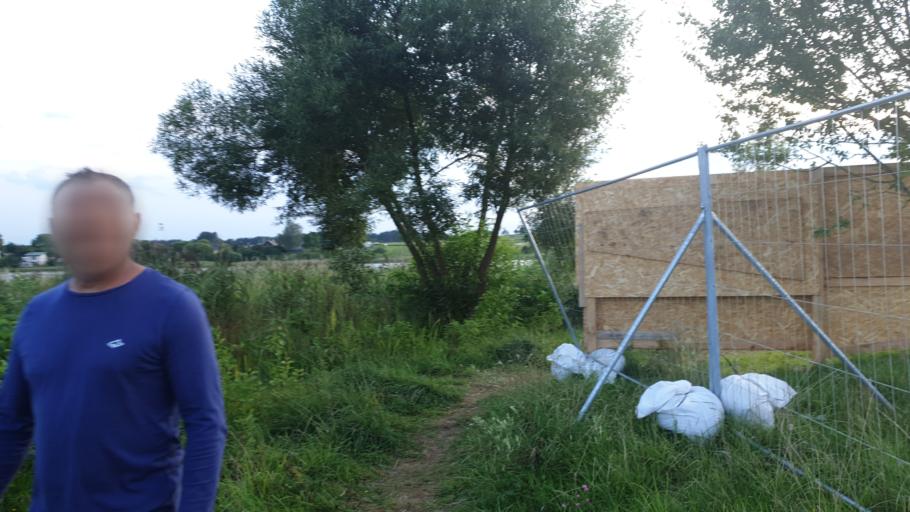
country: LT
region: Vilnius County
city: Pilaite
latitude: 54.7051
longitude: 25.1605
